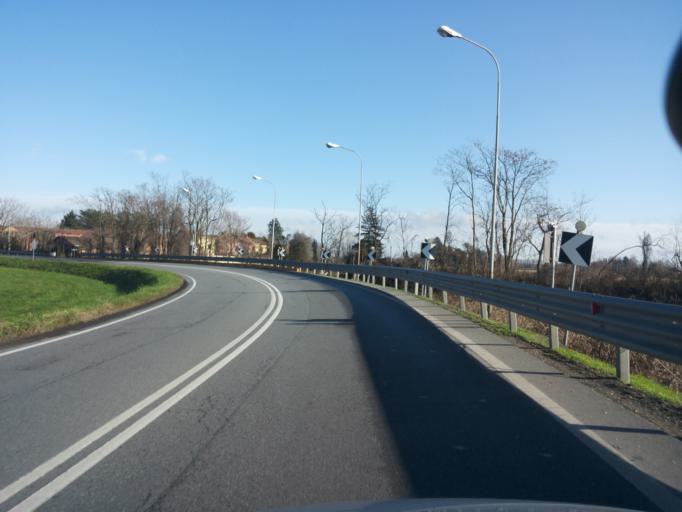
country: IT
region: Piedmont
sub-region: Provincia di Vercelli
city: Vercelli
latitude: 45.3265
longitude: 8.4458
